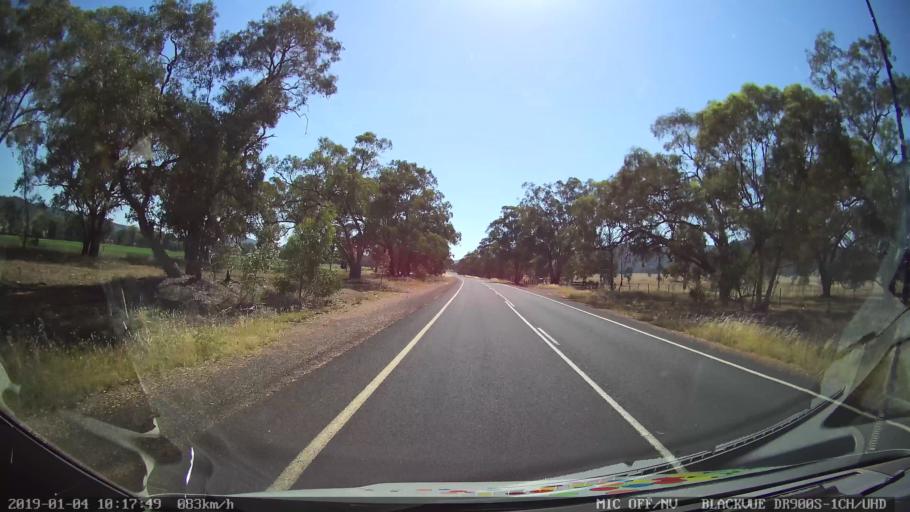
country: AU
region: New South Wales
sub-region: Cabonne
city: Canowindra
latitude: -33.3837
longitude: 148.4572
